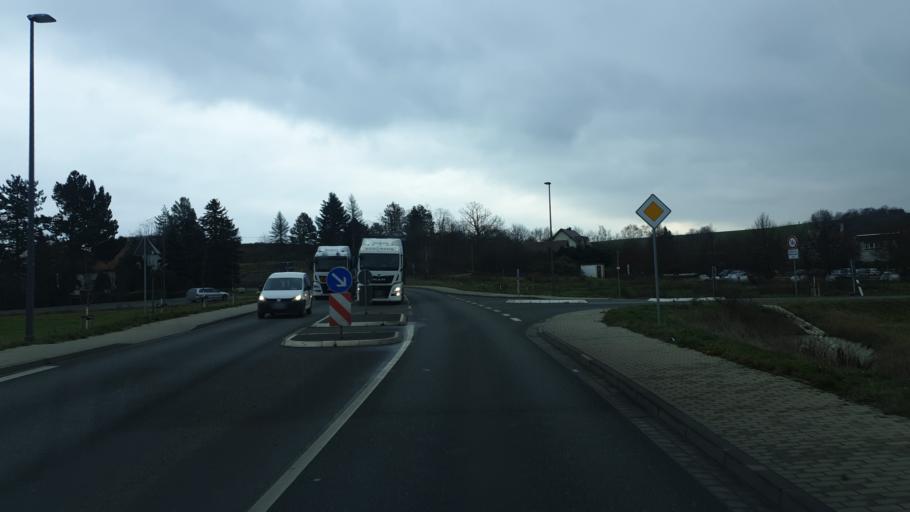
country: DE
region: Saxony-Anhalt
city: Wethau
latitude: 51.1342
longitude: 11.8648
